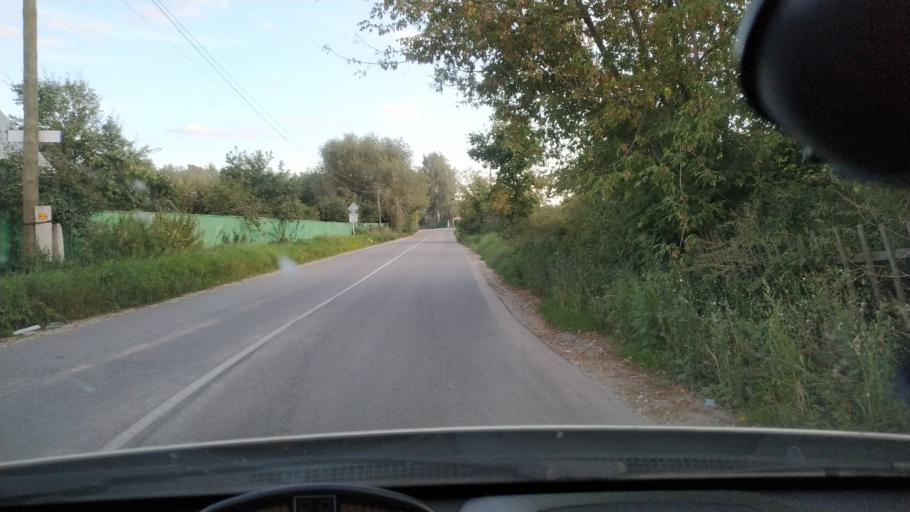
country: RU
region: Rjazan
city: Rybnoye
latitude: 54.8661
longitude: 39.6499
